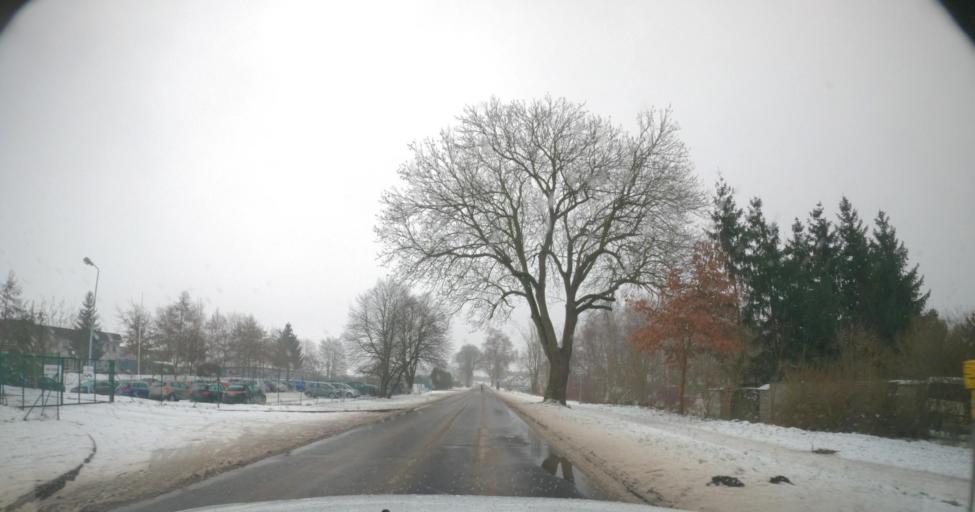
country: PL
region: West Pomeranian Voivodeship
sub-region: Powiat gryficki
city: Gryfice
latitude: 53.9128
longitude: 15.2178
